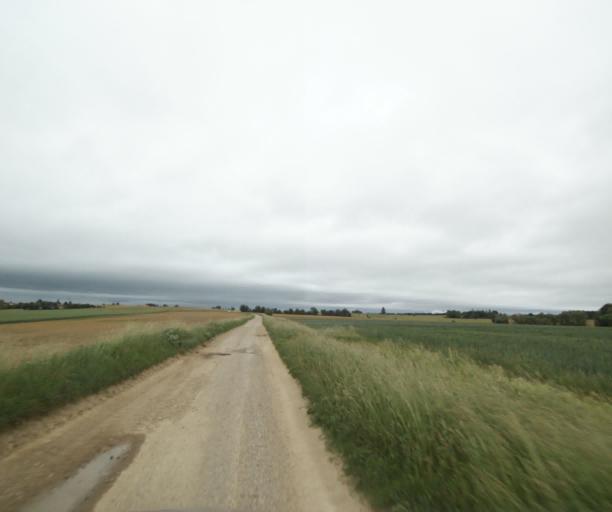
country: FR
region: Rhone-Alpes
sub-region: Departement de l'Ain
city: Miribel
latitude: 45.8417
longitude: 4.9338
